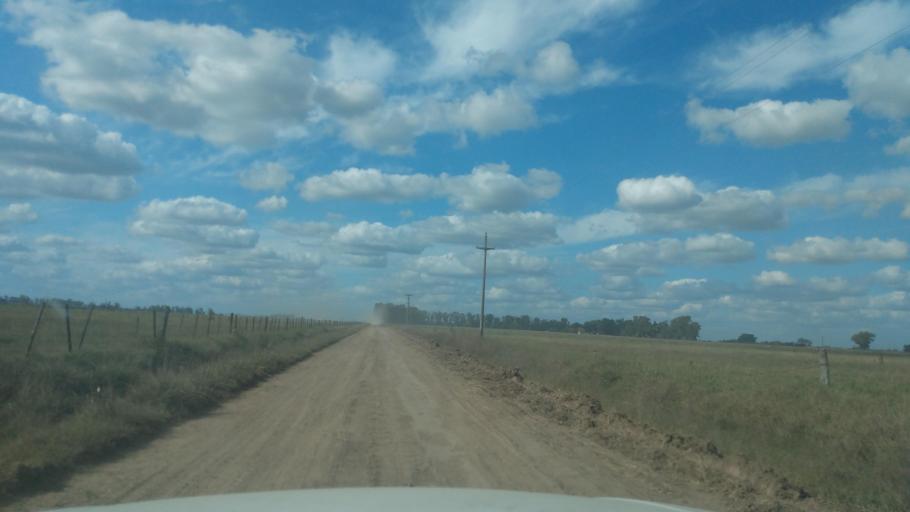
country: AR
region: Buenos Aires
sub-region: Partido de Navarro
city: Navarro
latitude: -35.0361
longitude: -59.5077
